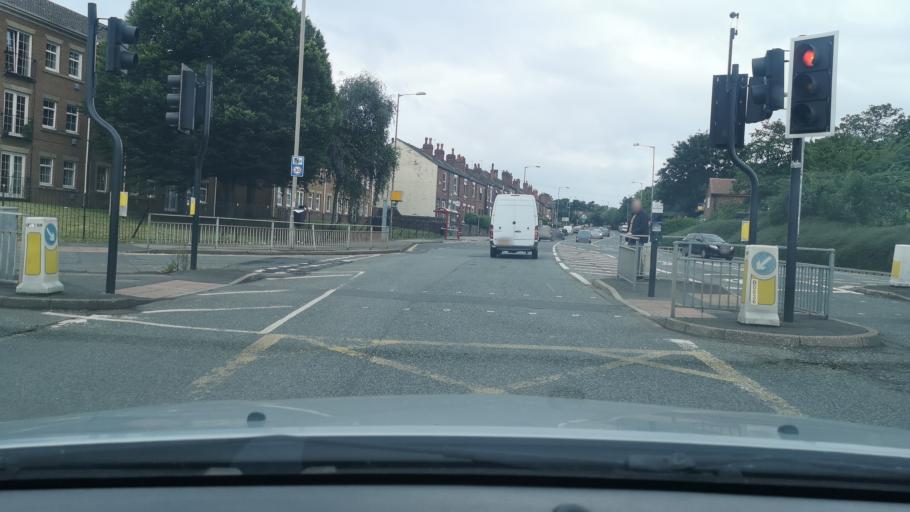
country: GB
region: England
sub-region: City and Borough of Wakefield
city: Wakefield
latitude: 53.6781
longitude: -1.5239
